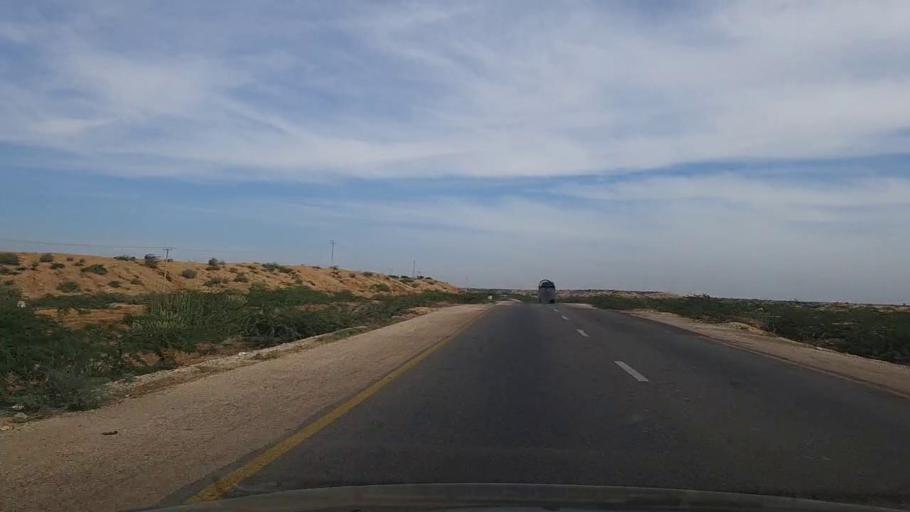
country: PK
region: Sindh
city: Thatta
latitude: 24.8538
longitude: 68.0188
